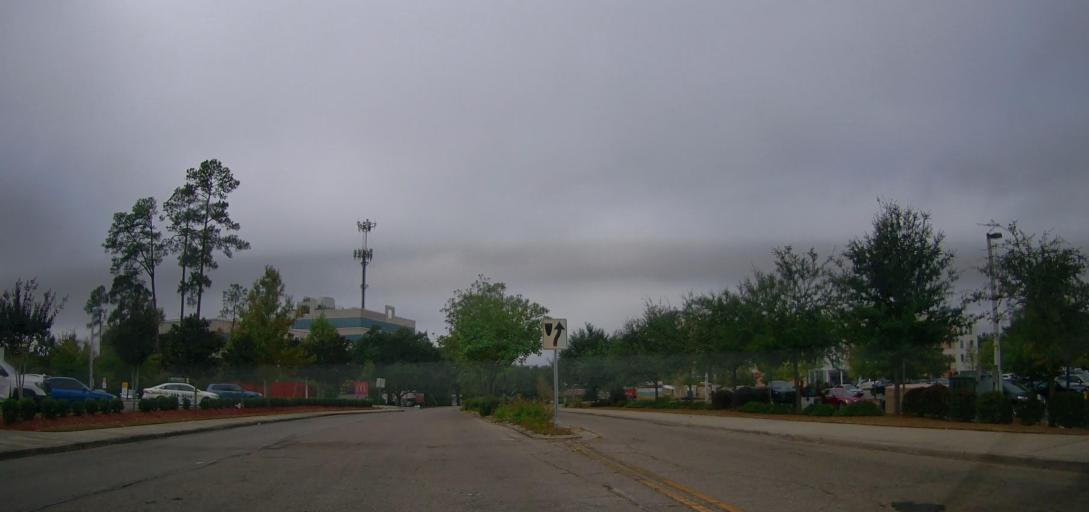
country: US
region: Florida
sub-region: Leon County
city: Tallahassee
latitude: 30.4397
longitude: -84.2622
